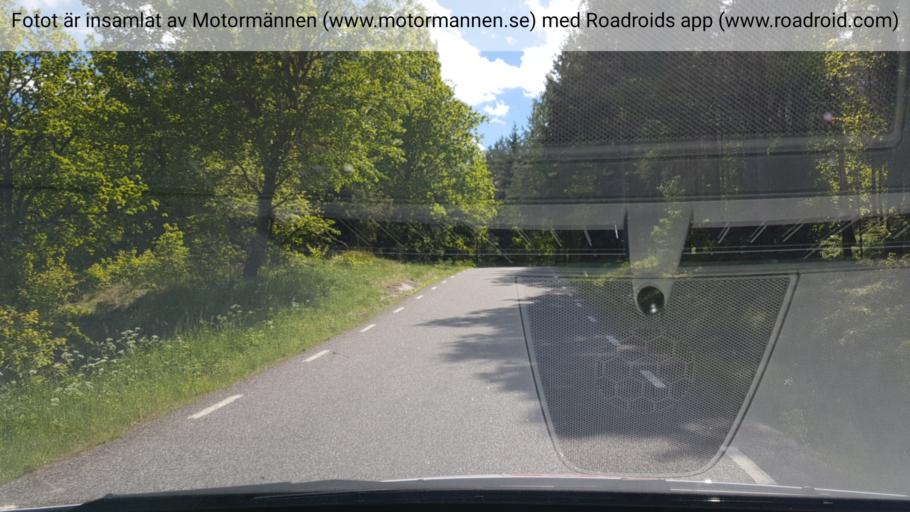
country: SE
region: Kalmar
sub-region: Vasterviks Kommun
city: Forserum
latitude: 57.9622
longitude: 16.6337
